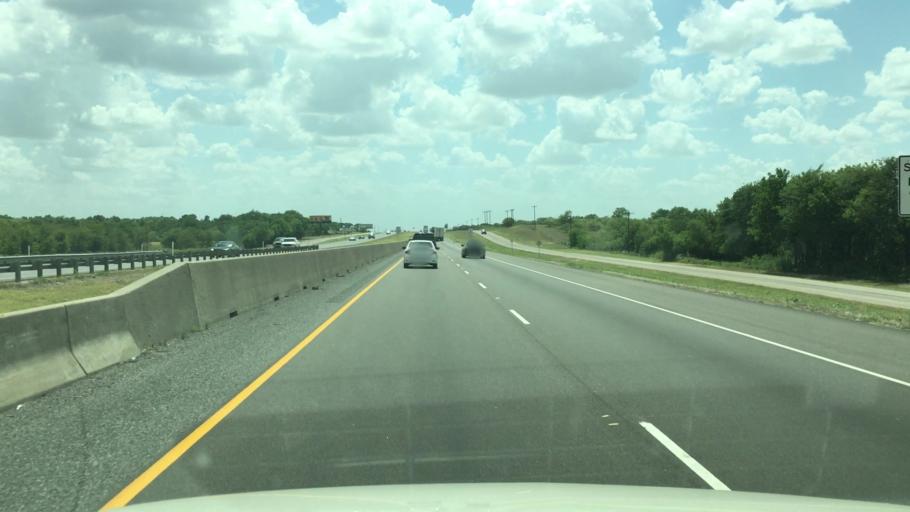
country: US
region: Texas
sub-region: Hunt County
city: Caddo Mills
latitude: 33.0142
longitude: -96.2134
